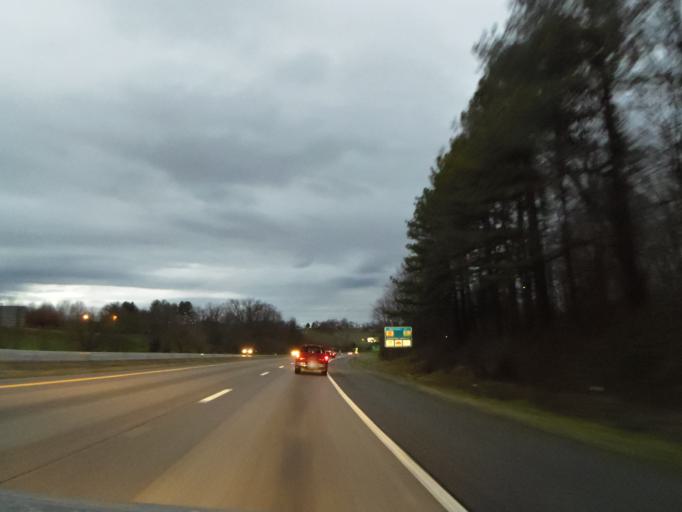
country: US
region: Tennessee
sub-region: Washington County
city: Oak Grove
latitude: 36.3636
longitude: -82.4095
